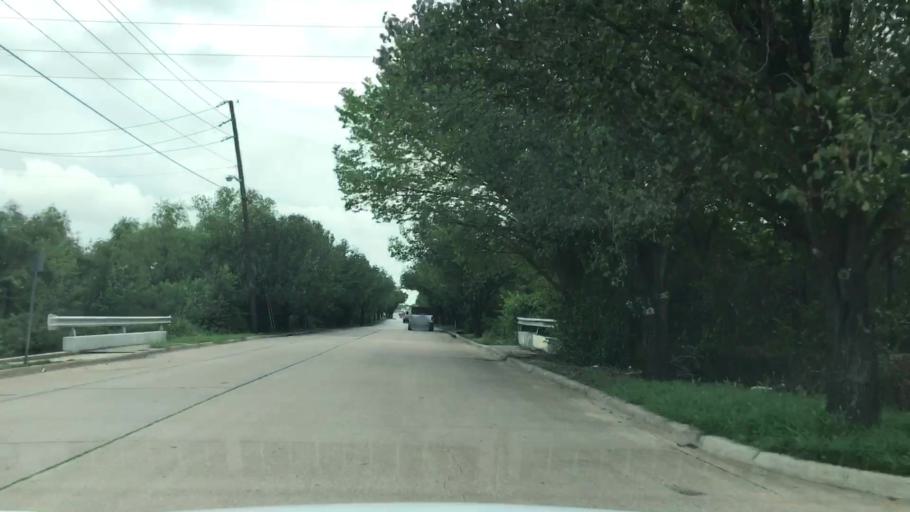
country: US
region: Texas
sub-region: Dallas County
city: Farmers Branch
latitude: 32.8837
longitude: -96.9006
